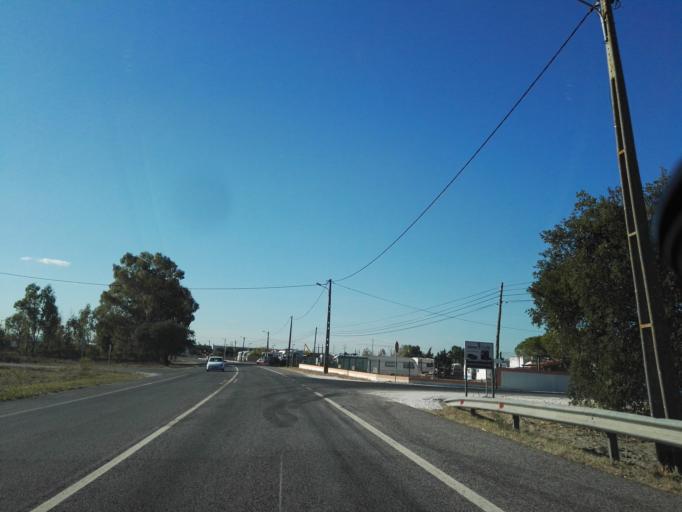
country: PT
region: Santarem
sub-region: Benavente
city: Samora Correia
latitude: 38.9096
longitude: -8.8470
